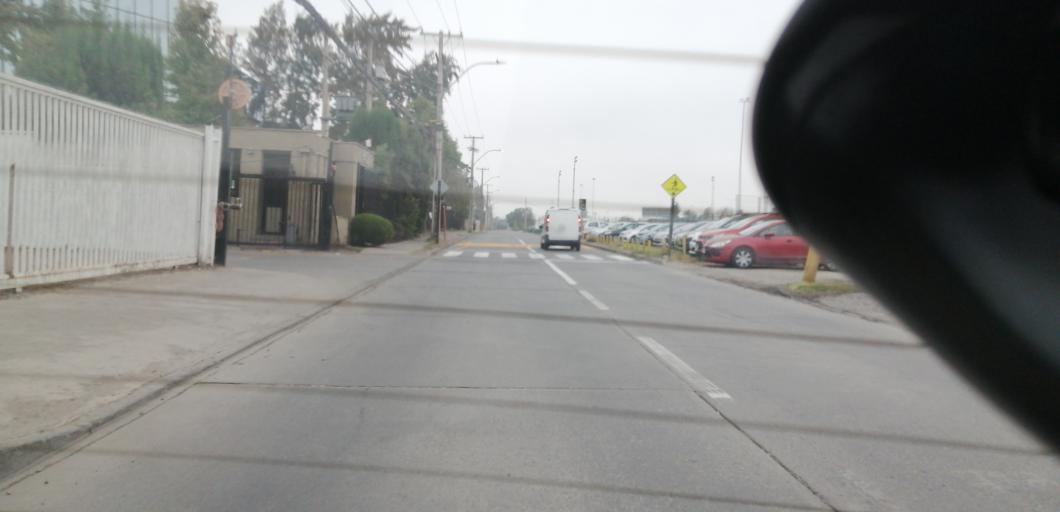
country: CL
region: Santiago Metropolitan
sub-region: Provincia de Santiago
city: Lo Prado
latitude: -33.4485
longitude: -70.7694
